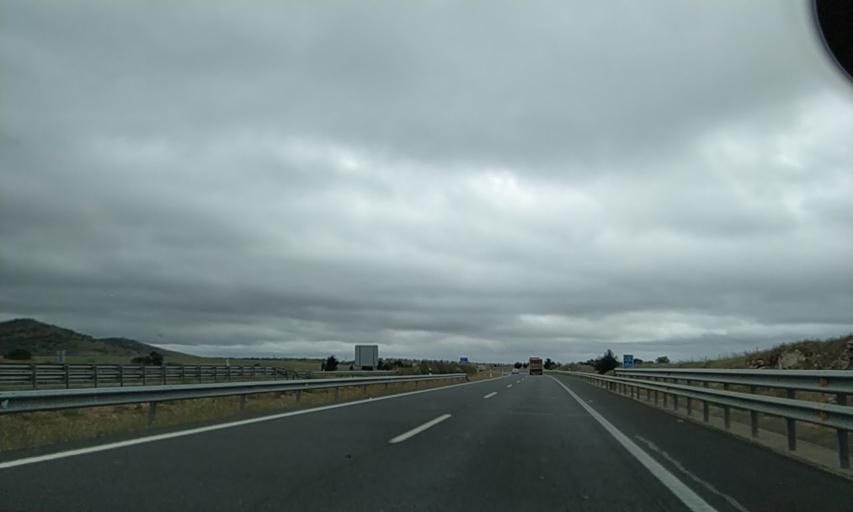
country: ES
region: Extremadura
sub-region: Provincia de Caceres
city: Caceres
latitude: 39.4445
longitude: -6.4131
